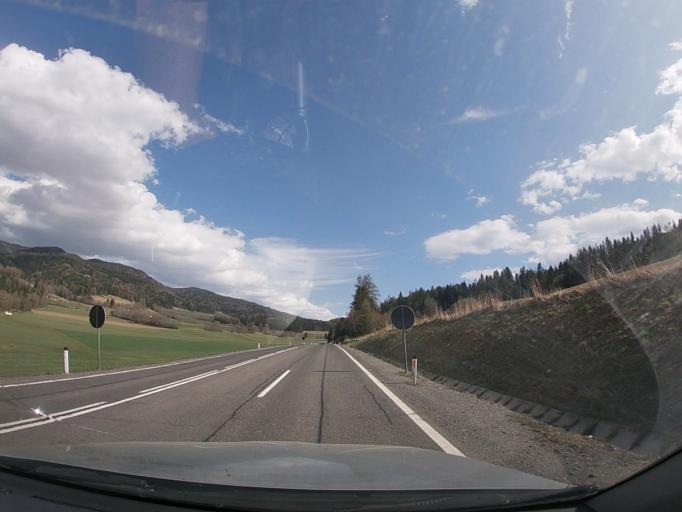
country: AT
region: Styria
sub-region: Politischer Bezirk Murau
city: Perchau am Sattel
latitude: 47.1166
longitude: 14.4529
